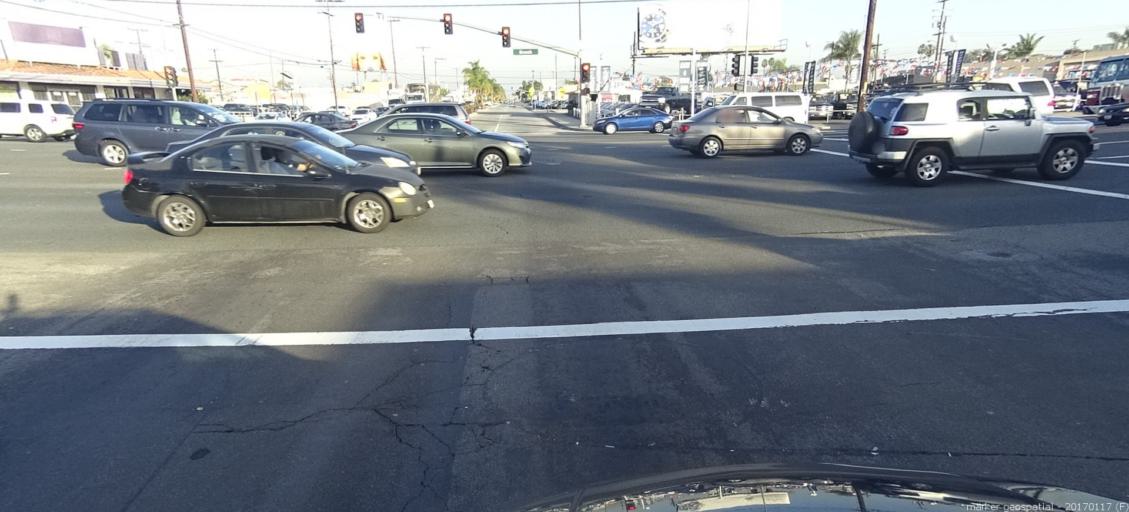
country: US
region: California
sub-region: Orange County
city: Midway City
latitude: 33.7446
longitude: -117.9898
